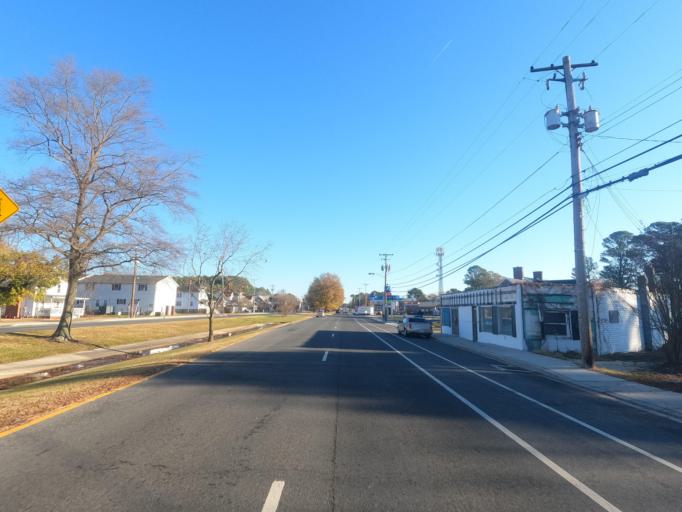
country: US
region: Maryland
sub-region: Somerset County
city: Crisfield
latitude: 37.9877
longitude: -75.8487
